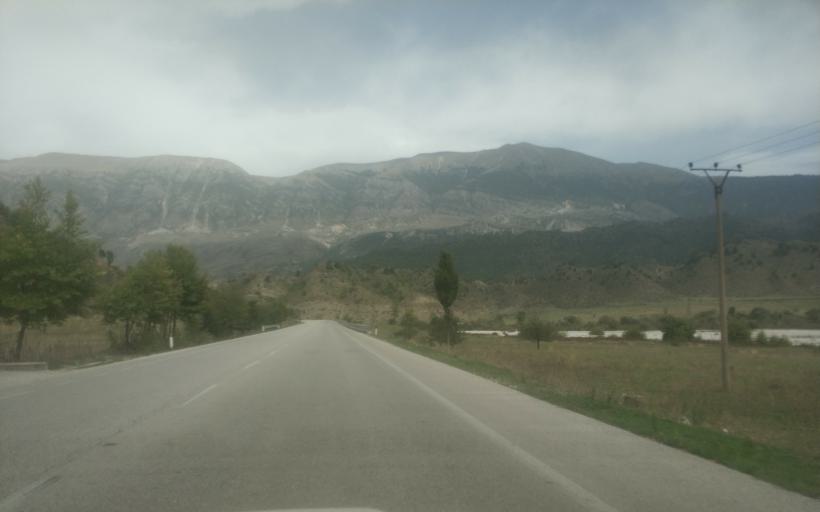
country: AL
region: Gjirokaster
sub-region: Rrethi i Gjirokastres
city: Picar
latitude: 40.1994
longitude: 20.0879
